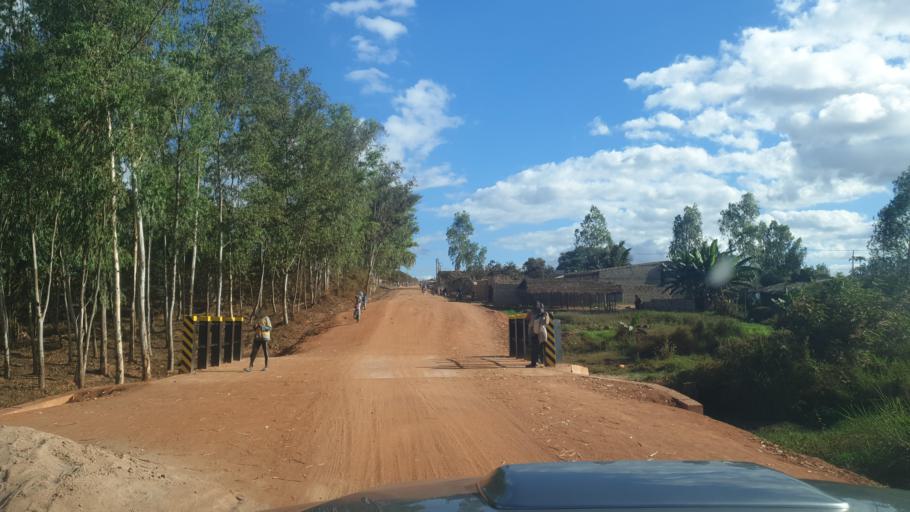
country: MZ
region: Nampula
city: Nampula
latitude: -15.0975
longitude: 39.2245
